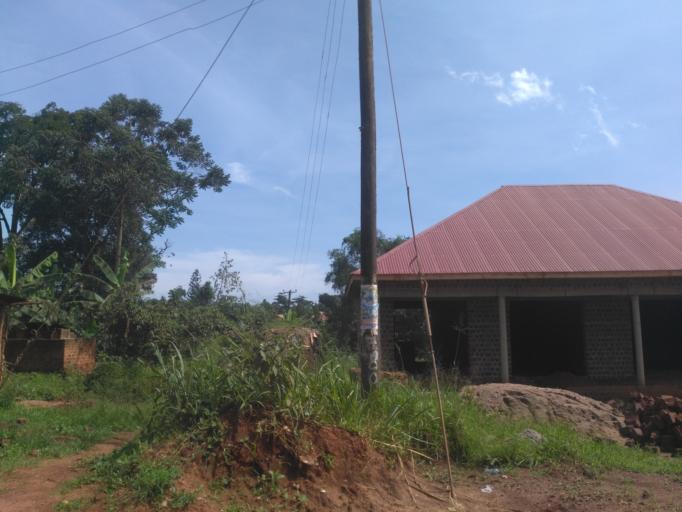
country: UG
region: Central Region
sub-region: Wakiso District
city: Kireka
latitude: 0.4465
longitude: 32.5811
